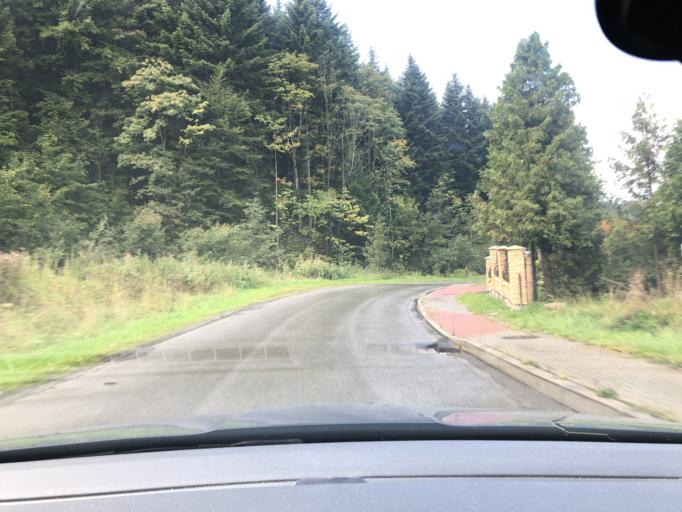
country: PL
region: Lesser Poland Voivodeship
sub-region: Powiat suski
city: Stryszawa
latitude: 49.7067
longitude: 19.5331
